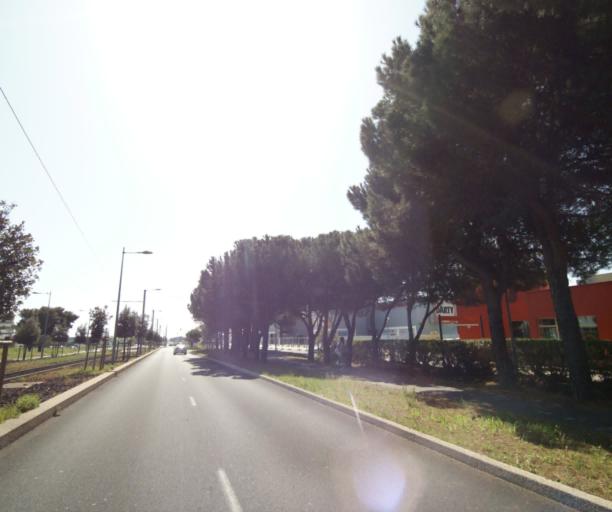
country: FR
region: Languedoc-Roussillon
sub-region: Departement de l'Herault
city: Perols
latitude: 43.5790
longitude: 3.9330
